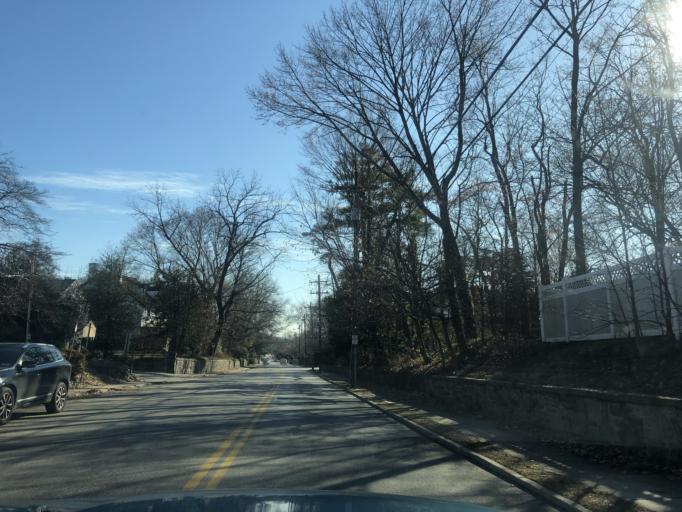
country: US
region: Pennsylvania
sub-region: Montgomery County
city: Bala-Cynwyd
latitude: 40.0013
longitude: -75.2396
